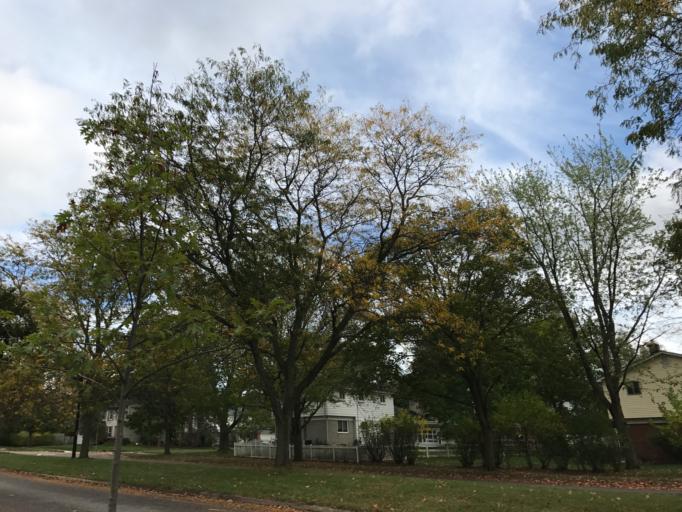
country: US
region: Michigan
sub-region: Washtenaw County
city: Ann Arbor
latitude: 42.2482
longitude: -83.7242
